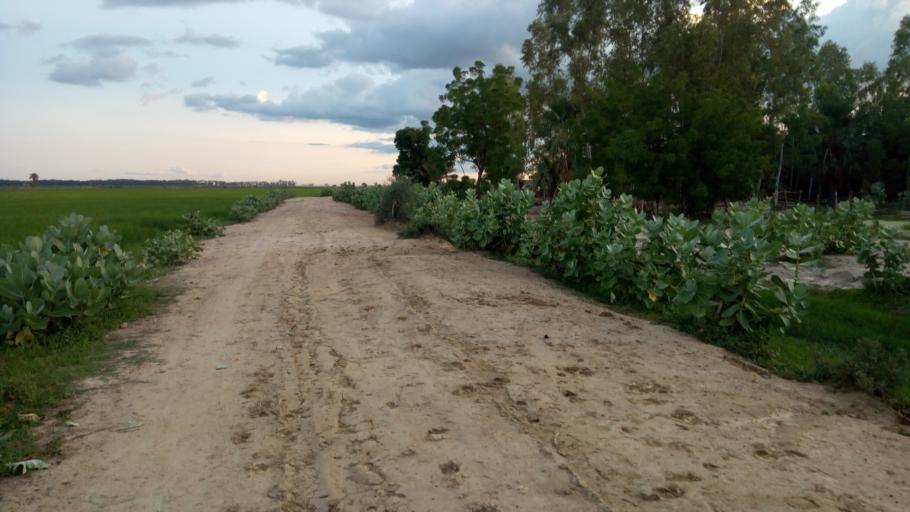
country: ML
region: Segou
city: Niono
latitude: 14.3097
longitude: -5.9543
